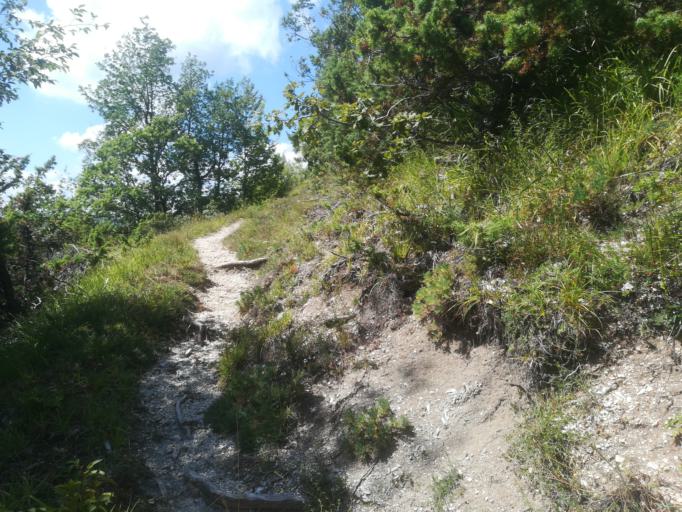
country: IT
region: Umbria
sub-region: Provincia di Perugia
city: Scheggino
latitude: 42.6747
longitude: 12.8584
